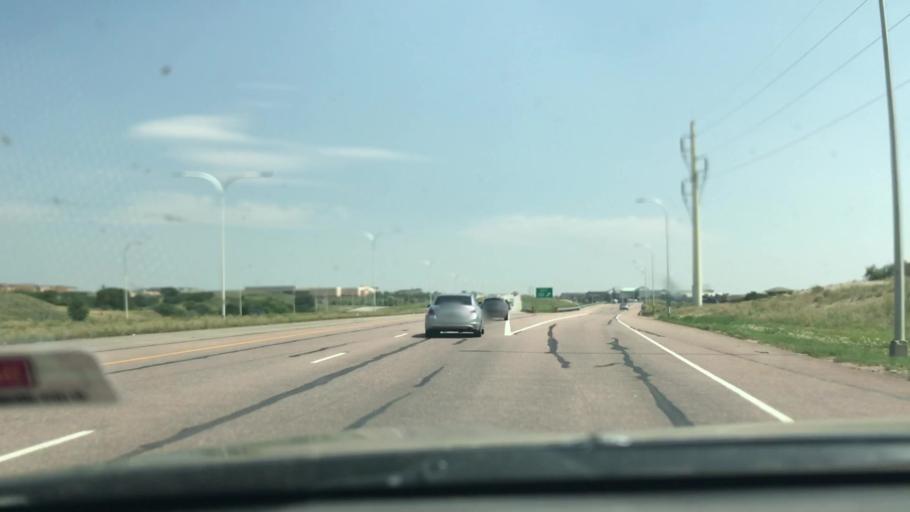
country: US
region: Colorado
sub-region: El Paso County
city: Black Forest
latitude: 38.9771
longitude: -104.7549
